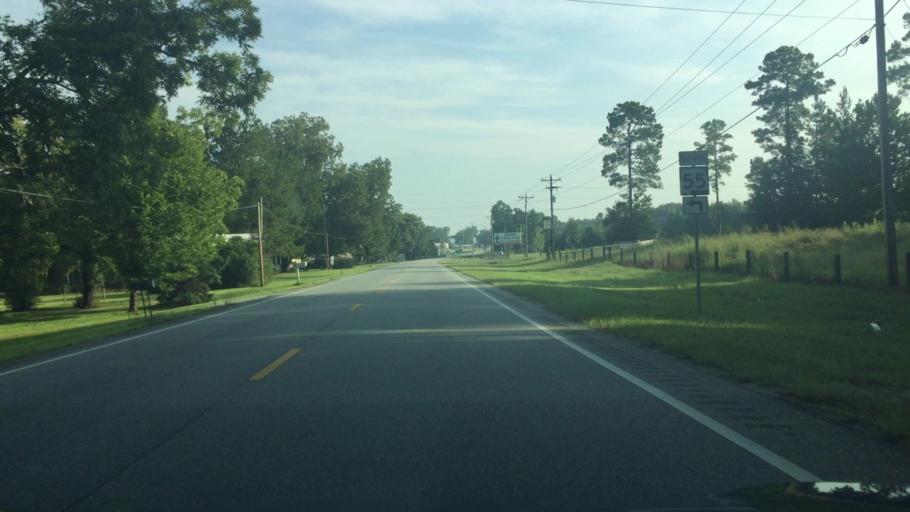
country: US
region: Alabama
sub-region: Covington County
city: Andalusia
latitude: 31.2727
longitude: -86.4743
